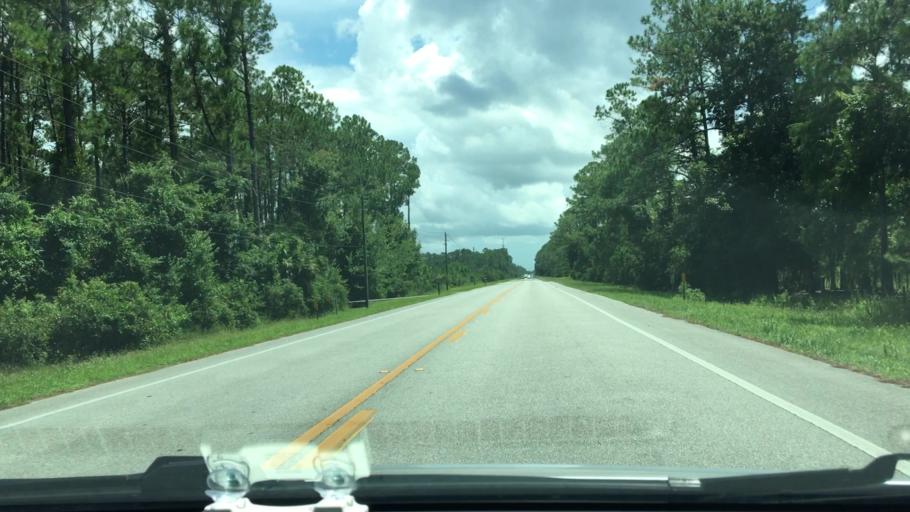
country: US
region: Florida
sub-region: Volusia County
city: Samsula-Spruce Creek
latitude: 29.0256
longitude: -81.0666
